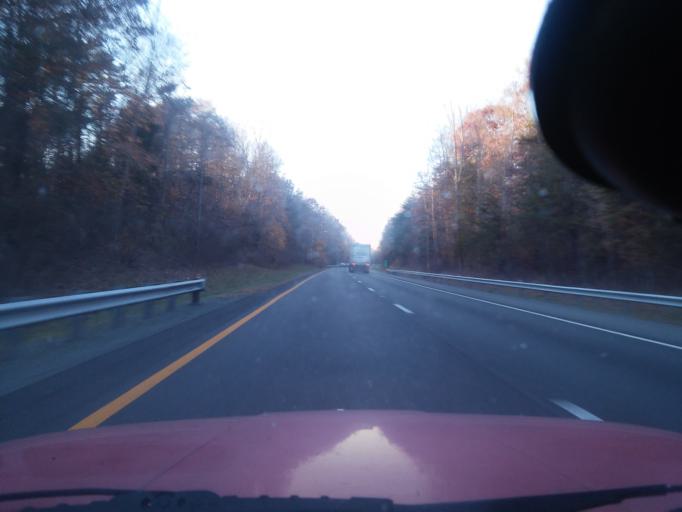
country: US
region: Virginia
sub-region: Goochland County
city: Goochland
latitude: 37.7224
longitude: -77.8155
